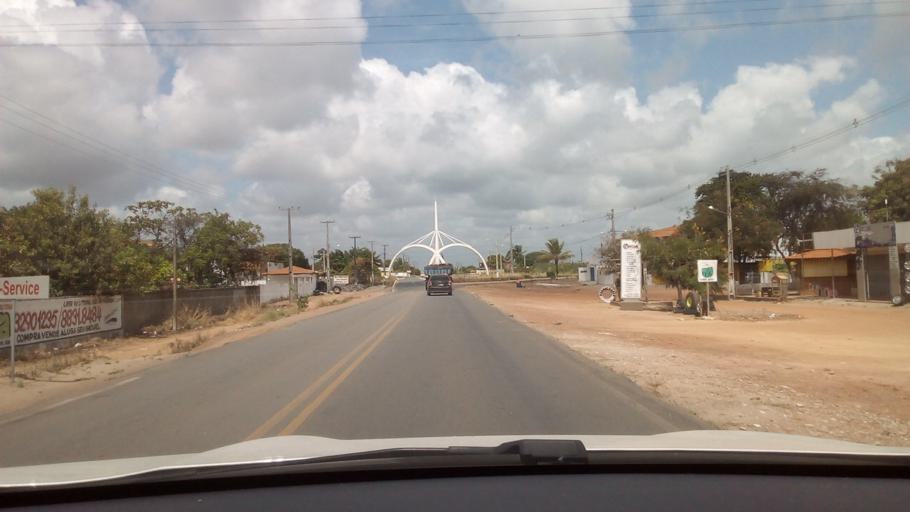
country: BR
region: Paraiba
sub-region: Conde
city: Conde
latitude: -7.2724
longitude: -34.8111
